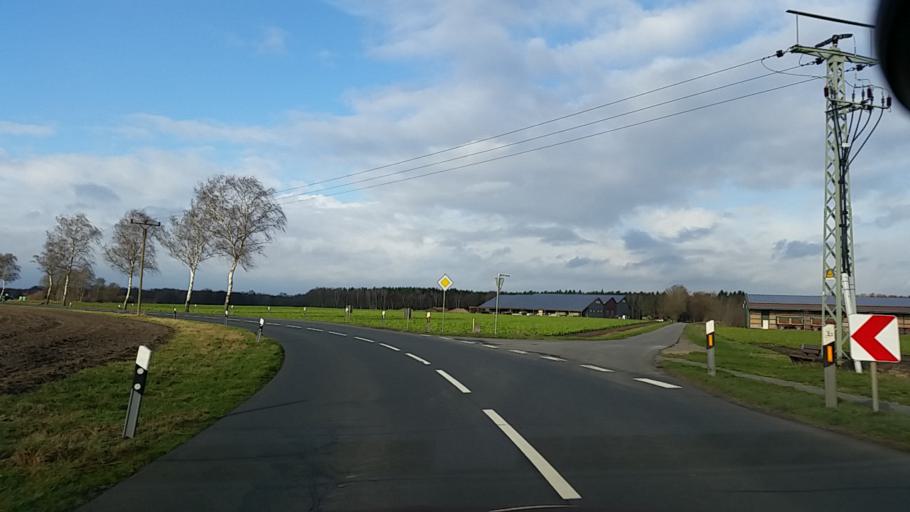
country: DE
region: Lower Saxony
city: Wrestedt
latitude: 52.9051
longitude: 10.5650
